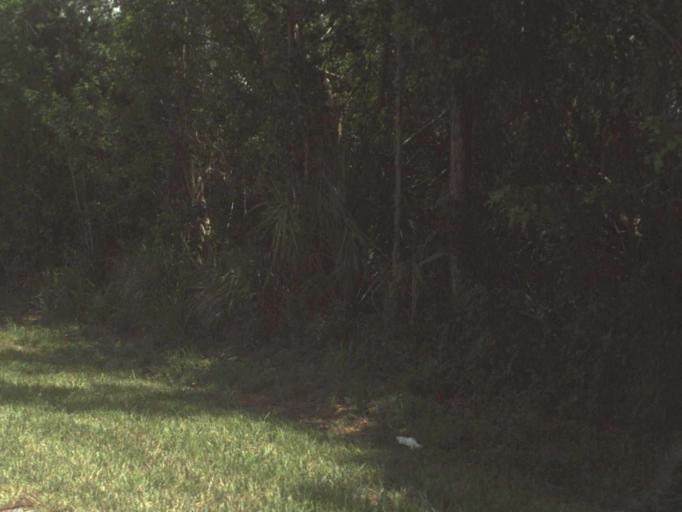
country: US
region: Florida
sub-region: Saint Lucie County
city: Fort Pierce South
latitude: 27.3744
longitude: -80.4230
